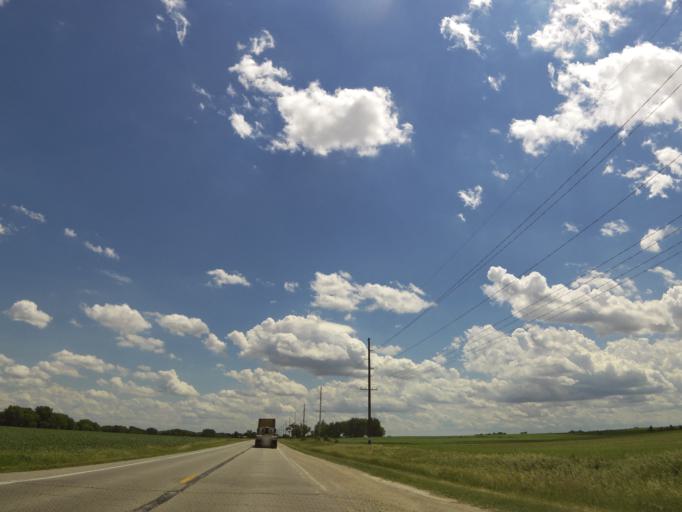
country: US
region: Iowa
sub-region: Buchanan County
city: Independence
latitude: 42.4073
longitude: -91.8899
